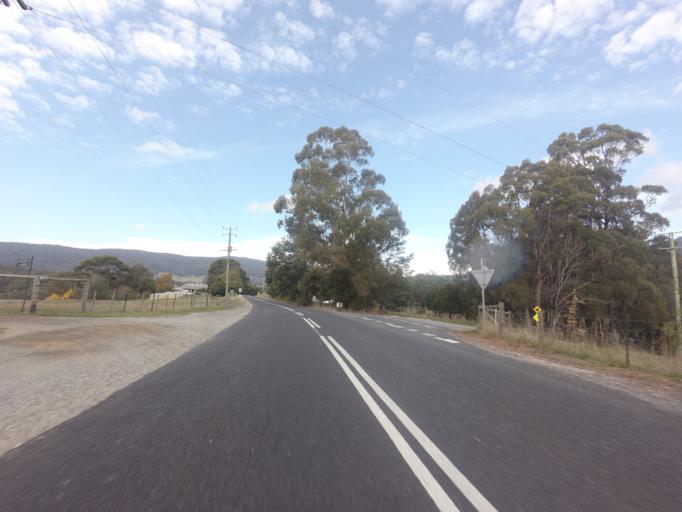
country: AU
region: Tasmania
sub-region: Meander Valley
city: Deloraine
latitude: -41.6211
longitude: 146.7006
